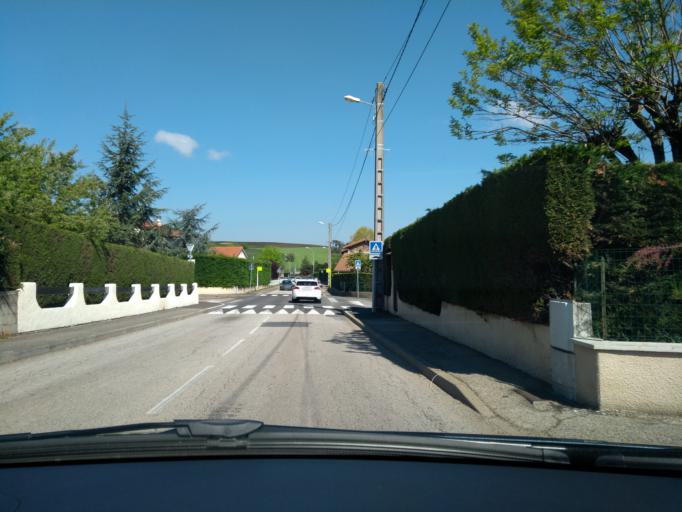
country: FR
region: Rhone-Alpes
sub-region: Departement de la Loire
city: Villars
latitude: 45.4645
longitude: 4.3446
